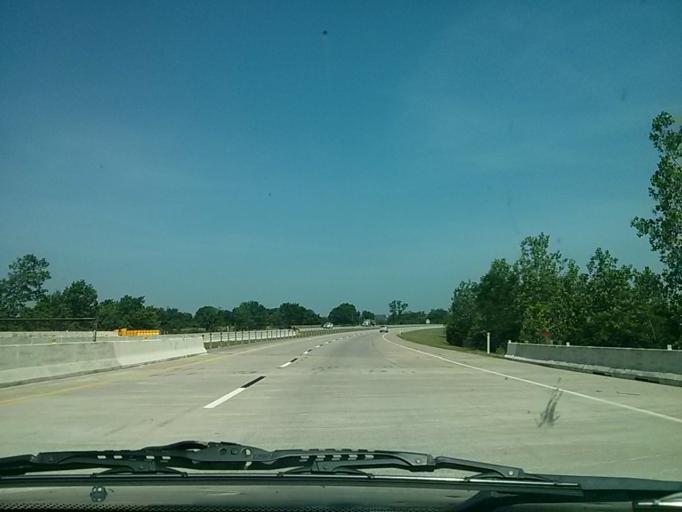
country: US
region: Oklahoma
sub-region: Creek County
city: Sapulpa
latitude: 36.0210
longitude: -96.0711
